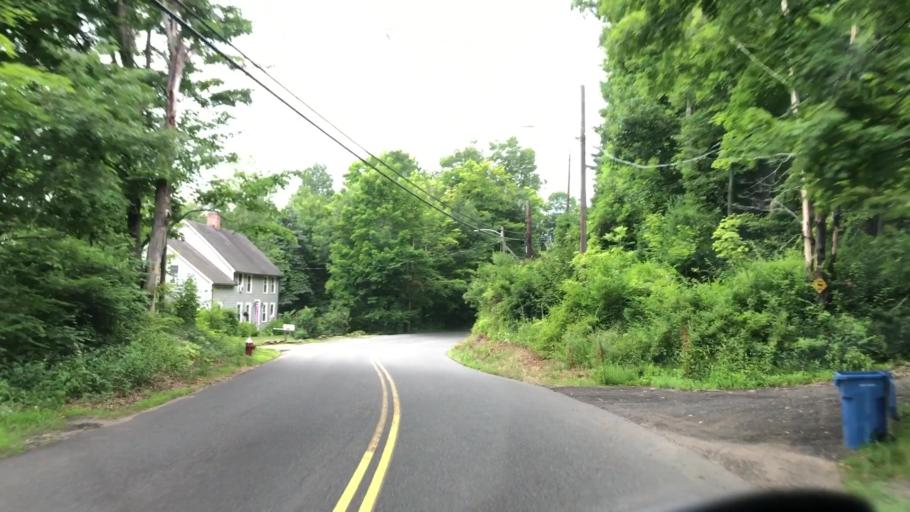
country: US
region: Massachusetts
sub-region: Hampden County
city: Holyoke
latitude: 42.1950
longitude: -72.6767
